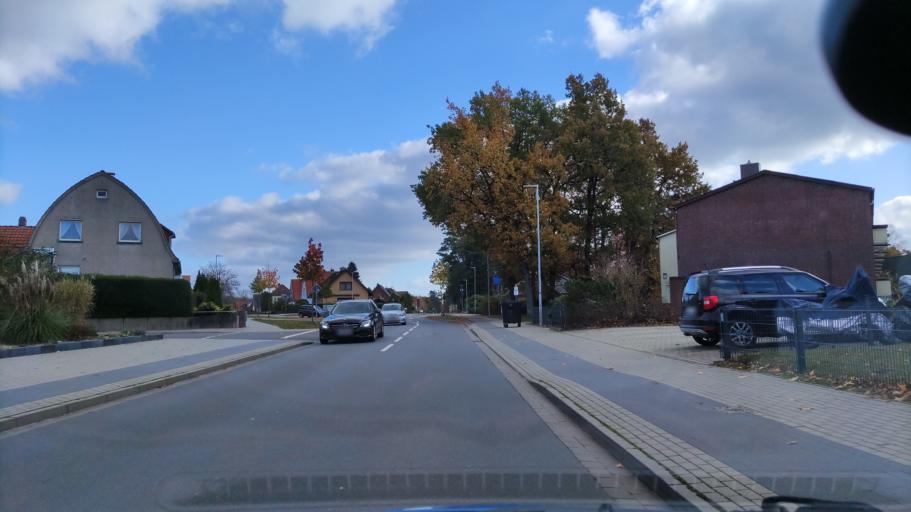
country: DE
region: Lower Saxony
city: Munster
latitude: 52.9864
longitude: 10.0998
